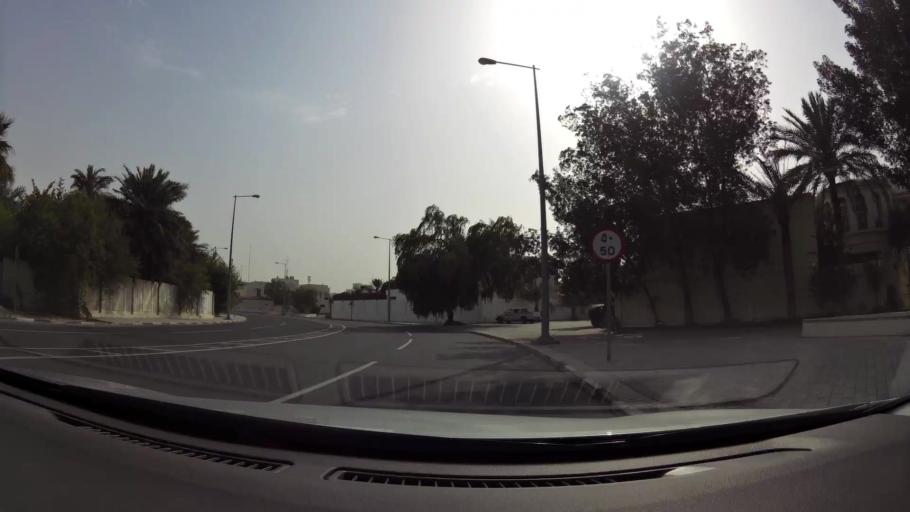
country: QA
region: Baladiyat ad Dawhah
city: Doha
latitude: 25.3256
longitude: 51.5068
